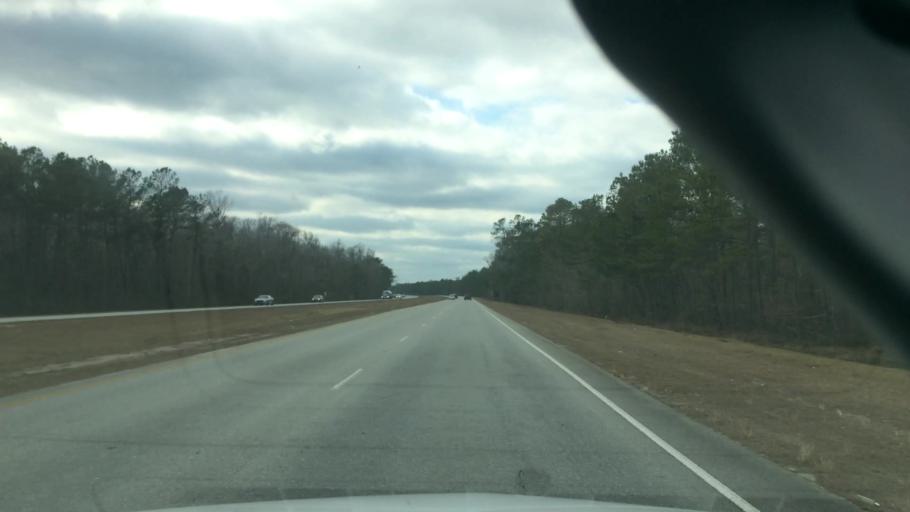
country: US
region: North Carolina
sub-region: Brunswick County
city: Bolivia
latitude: 34.0766
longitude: -78.1515
